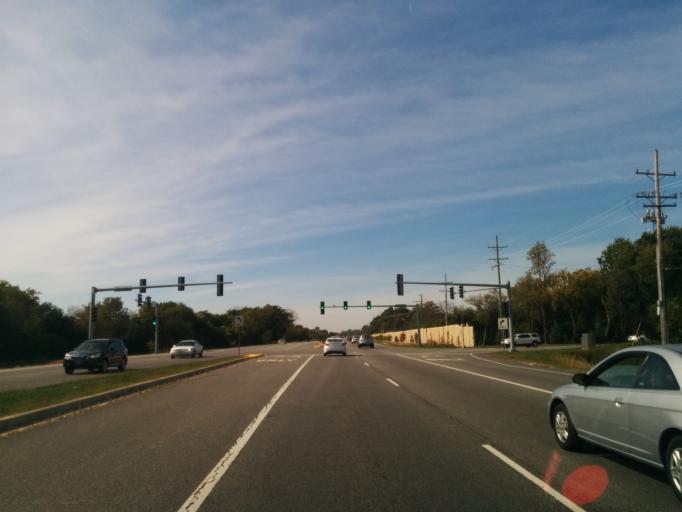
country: US
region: Illinois
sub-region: DuPage County
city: Wheaton
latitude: 41.8290
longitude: -88.1249
